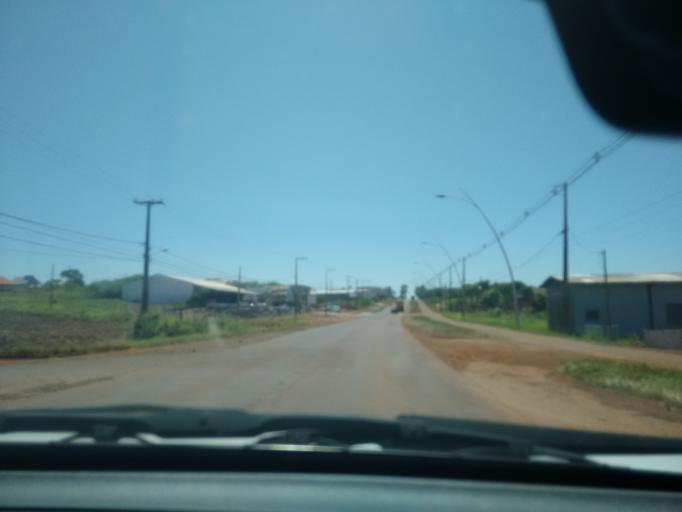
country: BR
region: Parana
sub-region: Marechal Candido Rondon
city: Marechal Candido Rondon
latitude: -24.5567
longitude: -54.0908
